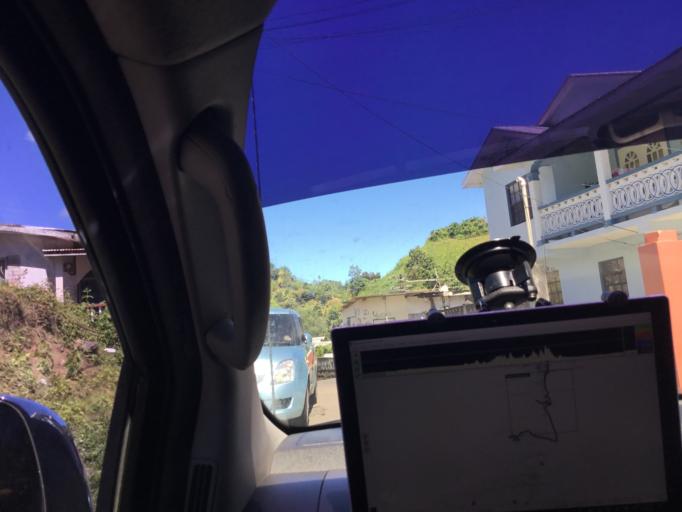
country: VC
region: Charlotte
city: Byera Village
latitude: 13.2446
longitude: -61.1409
